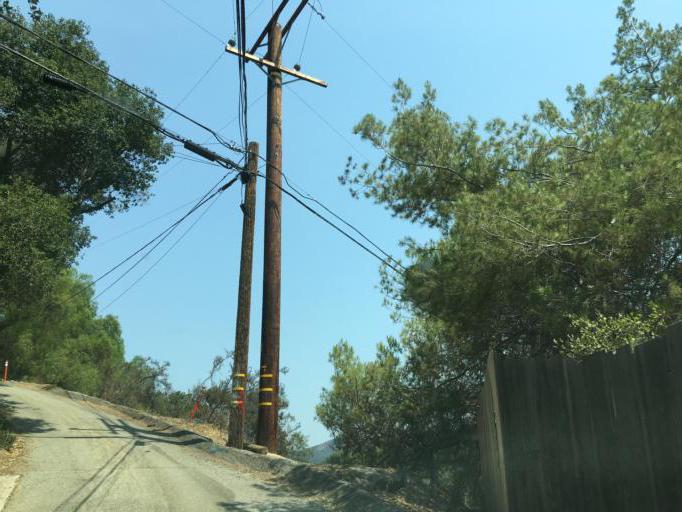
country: US
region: California
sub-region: Los Angeles County
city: Topanga
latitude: 34.0968
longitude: -118.6016
